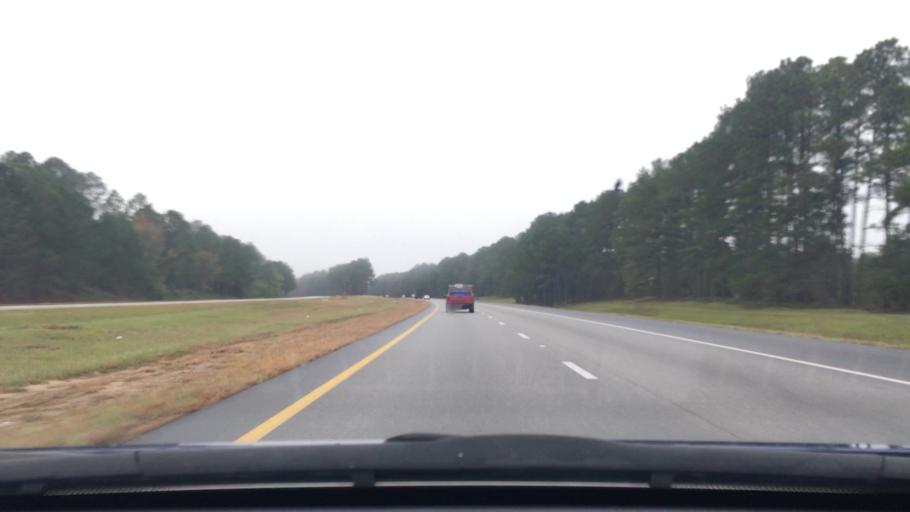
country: US
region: South Carolina
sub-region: Lee County
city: Bishopville
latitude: 34.2002
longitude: -80.3464
